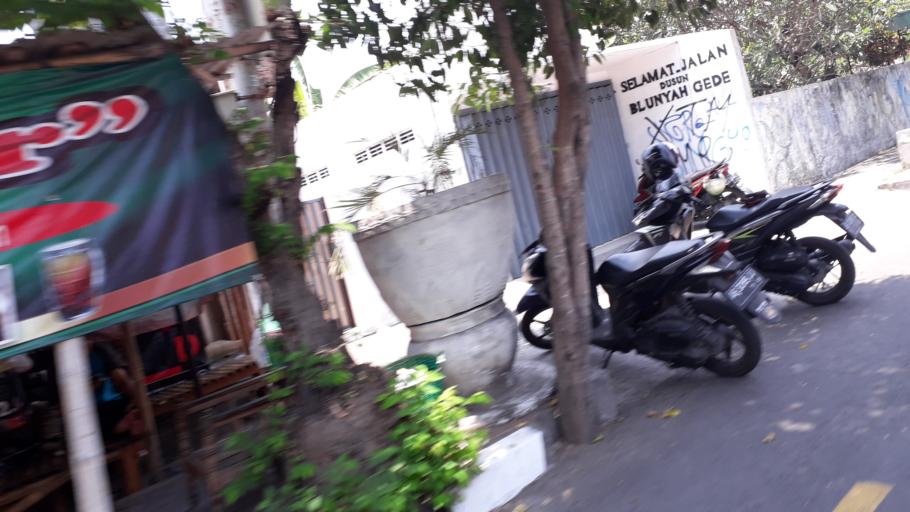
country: ID
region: Daerah Istimewa Yogyakarta
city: Yogyakarta
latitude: -7.7709
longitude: 110.3685
